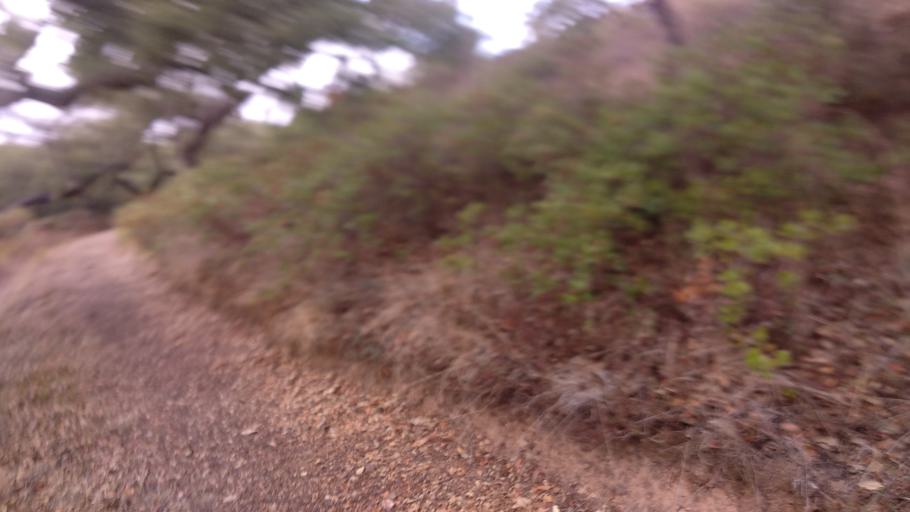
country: PT
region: Faro
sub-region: Sao Bras de Alportel
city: Sao Bras de Alportel
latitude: 37.1620
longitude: -7.9065
